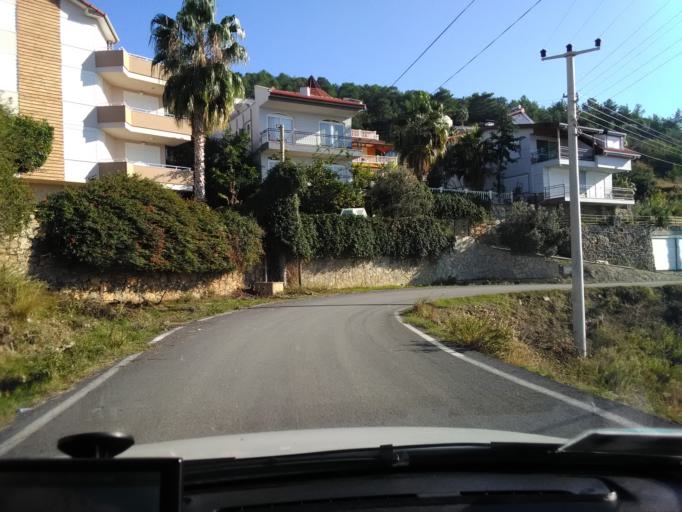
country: TR
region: Antalya
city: Gazipasa
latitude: 36.2370
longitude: 32.3028
